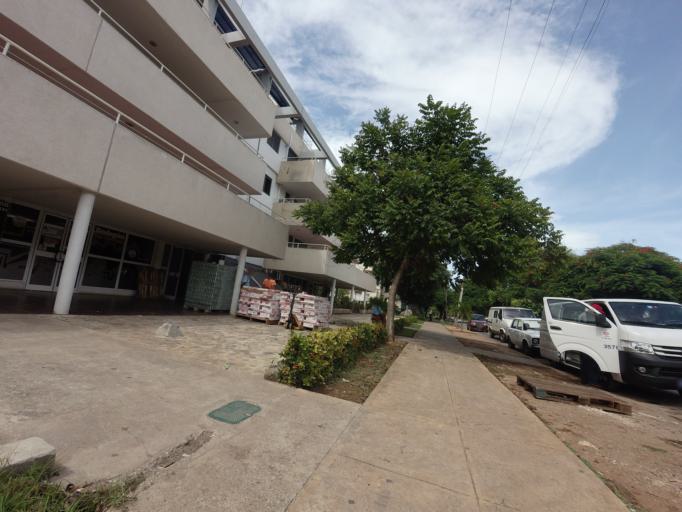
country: CU
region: La Habana
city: Havana
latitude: 23.1169
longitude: -82.4244
